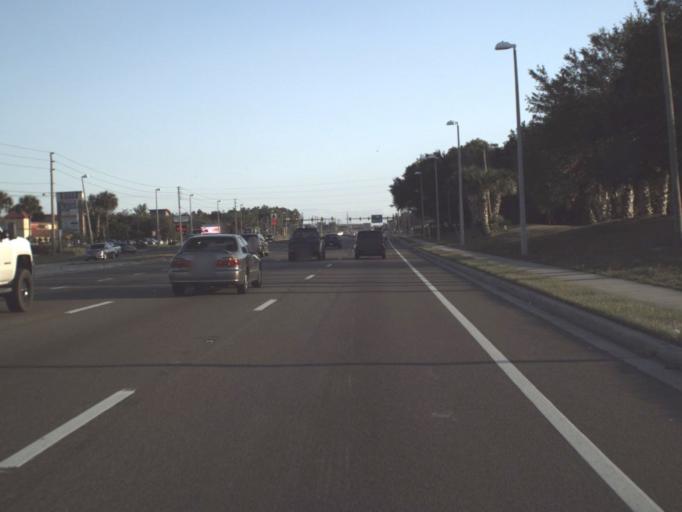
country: US
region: Florida
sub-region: Orange County
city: Southchase
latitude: 28.3865
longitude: -81.4047
